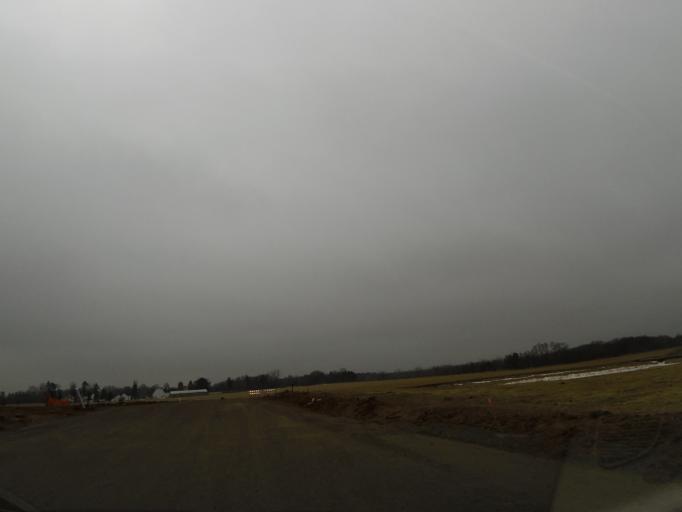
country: US
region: Minnesota
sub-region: Washington County
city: Lake Elmo
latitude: 45.0052
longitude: -92.8860
